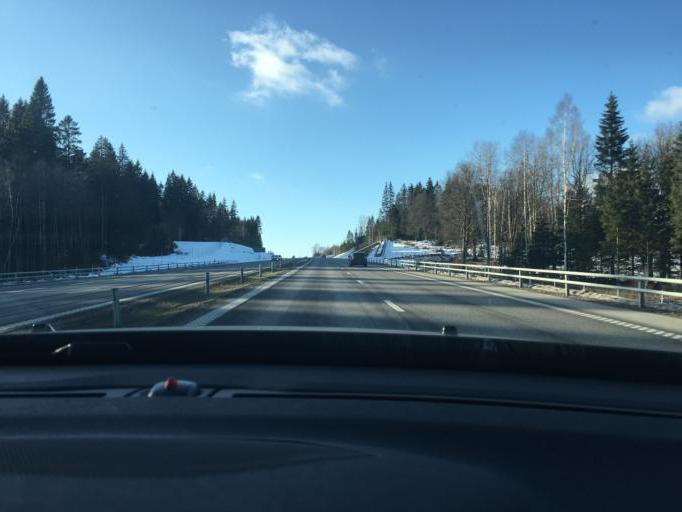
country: SE
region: Vaestra Goetaland
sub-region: Ulricehamns Kommun
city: Ulricehamn
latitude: 57.8191
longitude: 13.3377
